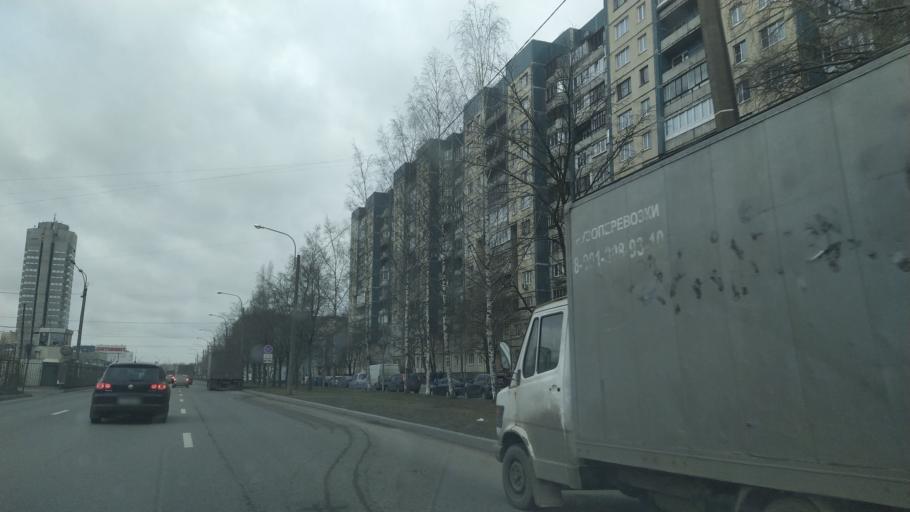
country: RU
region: St.-Petersburg
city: Komendantsky aerodrom
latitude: 60.0095
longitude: 30.2744
